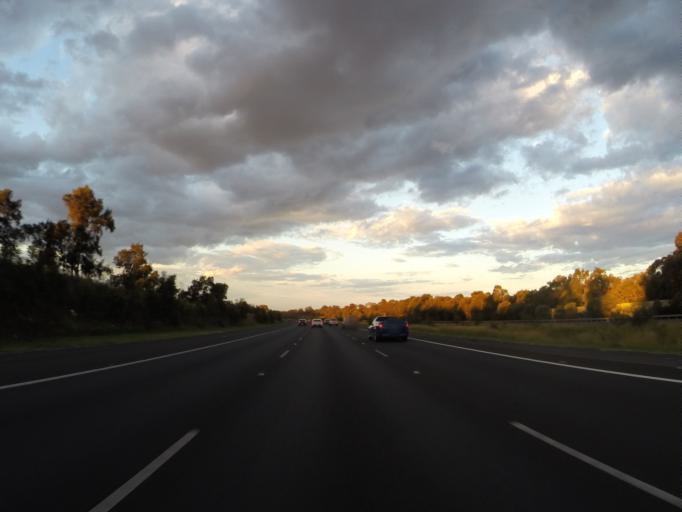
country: AU
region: New South Wales
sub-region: Campbelltown Municipality
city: Campbelltown
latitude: -34.0508
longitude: 150.8127
